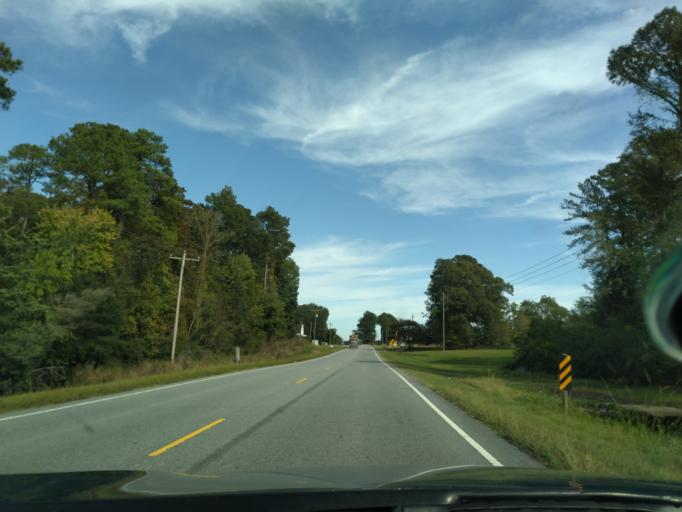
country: US
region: North Carolina
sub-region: Beaufort County
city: River Road
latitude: 35.5228
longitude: -76.8096
